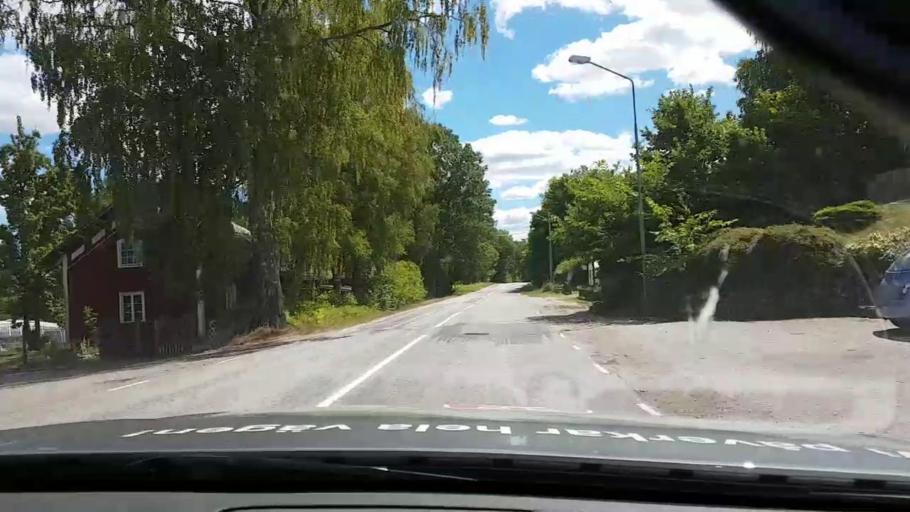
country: SE
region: Kalmar
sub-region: Vasterviks Kommun
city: Forserum
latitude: 58.0059
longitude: 16.4856
